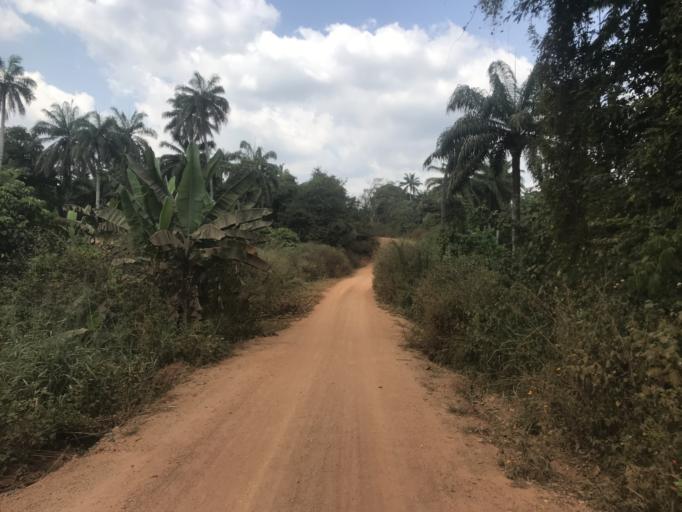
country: NG
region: Osun
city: Inisa
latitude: 7.8647
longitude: 4.3841
